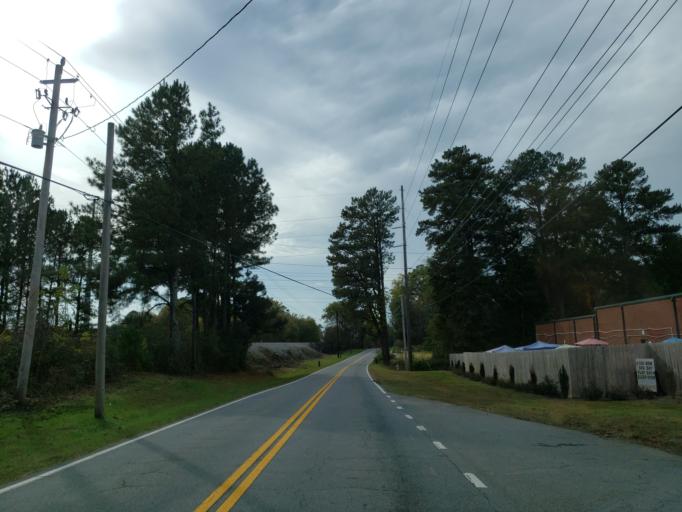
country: US
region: Georgia
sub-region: Cobb County
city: Acworth
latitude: 34.0633
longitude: -84.6504
